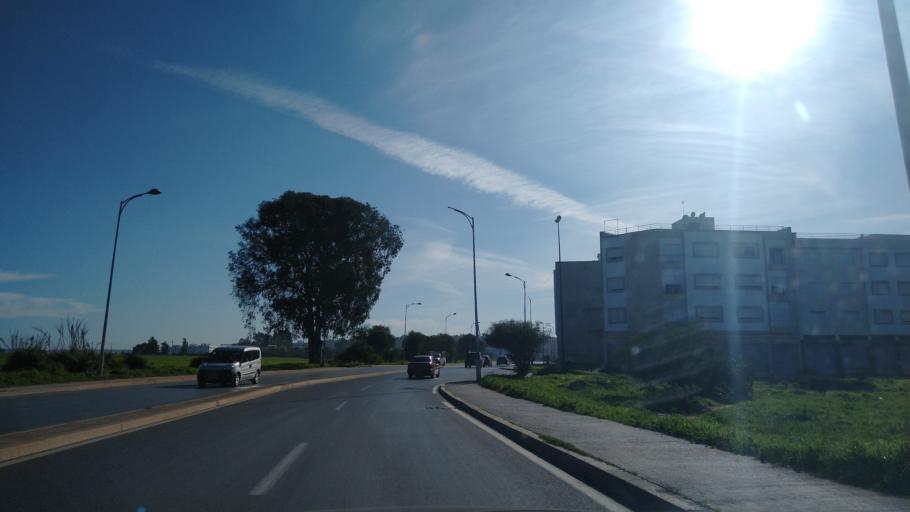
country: MA
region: Rabat-Sale-Zemmour-Zaer
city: Sale
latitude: 34.0173
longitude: -6.7348
